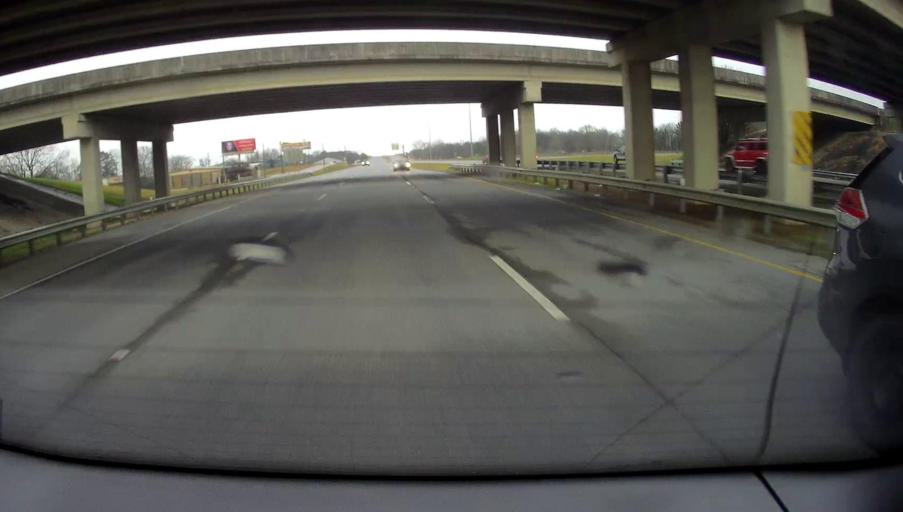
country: US
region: Alabama
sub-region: Morgan County
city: Decatur
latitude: 34.6014
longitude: -87.0315
